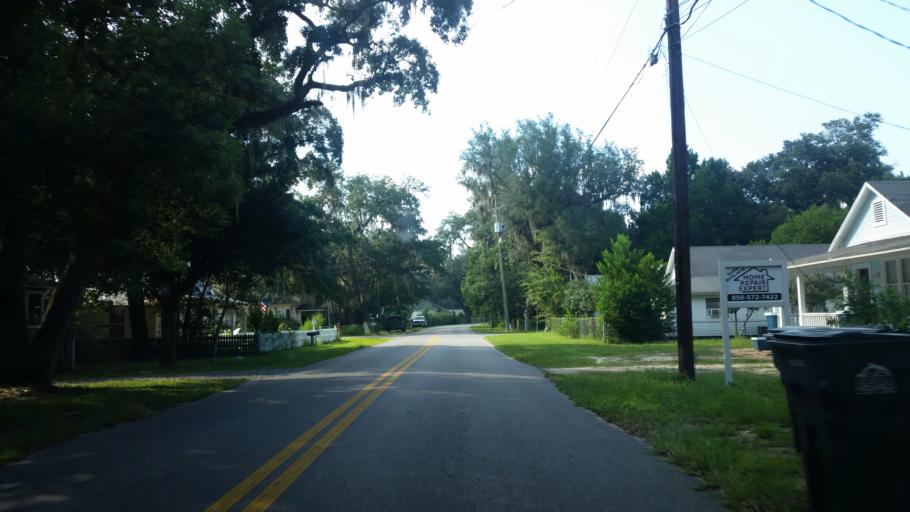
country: US
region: Florida
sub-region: Santa Rosa County
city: Bagdad
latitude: 30.5994
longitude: -87.0330
